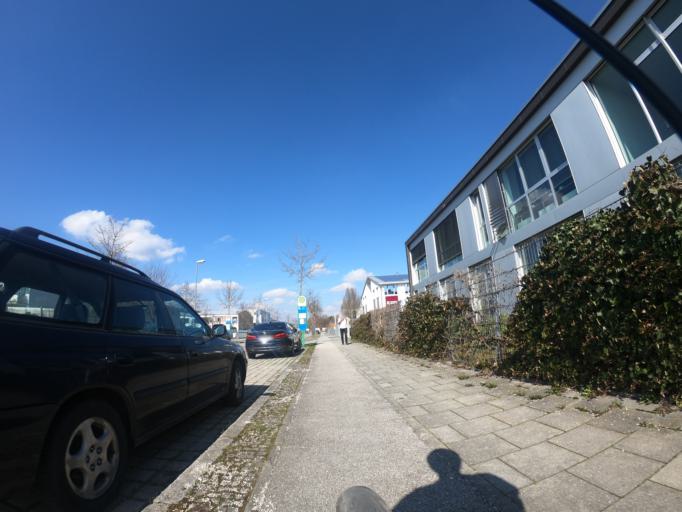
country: DE
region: Bavaria
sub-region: Upper Bavaria
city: Fuerstenfeldbruck
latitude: 48.1977
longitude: 11.2525
